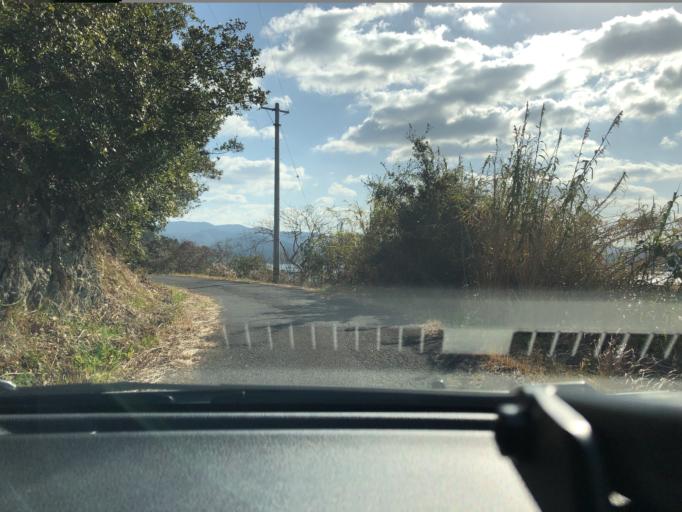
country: JP
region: Kochi
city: Sukumo
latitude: 32.9129
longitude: 132.6895
